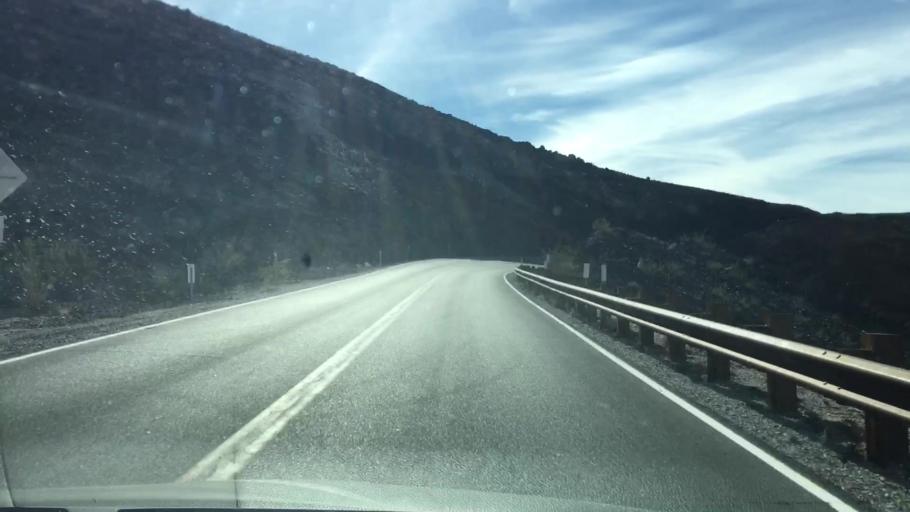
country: US
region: California
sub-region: San Bernardino County
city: Searles Valley
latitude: 36.3429
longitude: -117.5061
